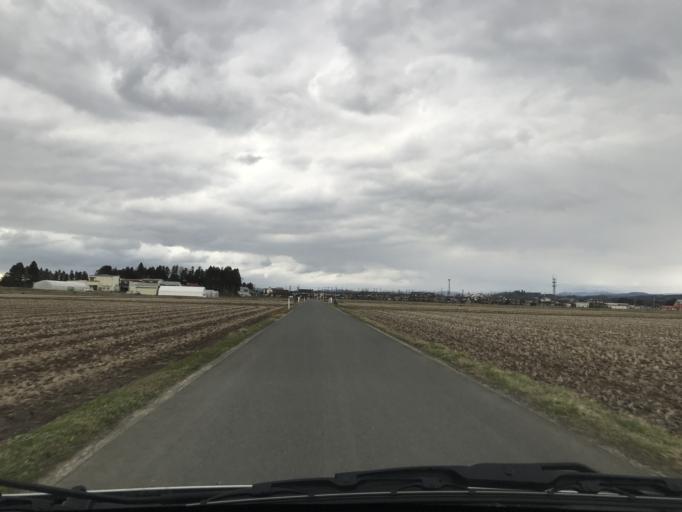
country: JP
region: Iwate
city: Mizusawa
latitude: 39.1091
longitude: 141.1639
